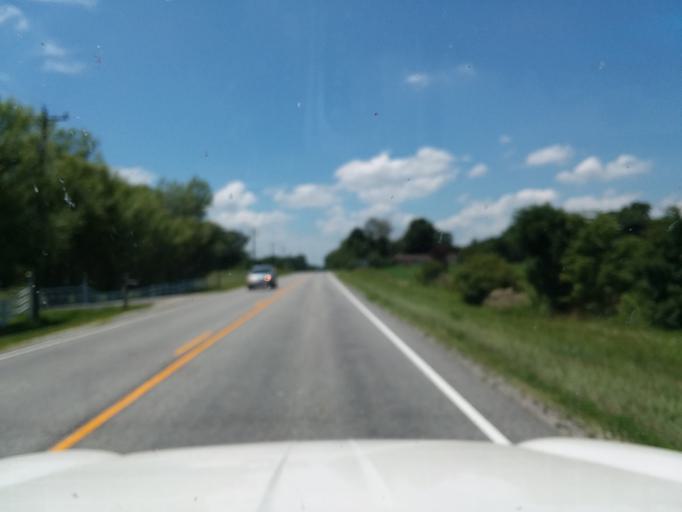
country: US
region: Indiana
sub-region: Johnson County
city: Trafalgar
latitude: 39.4092
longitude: -86.1068
